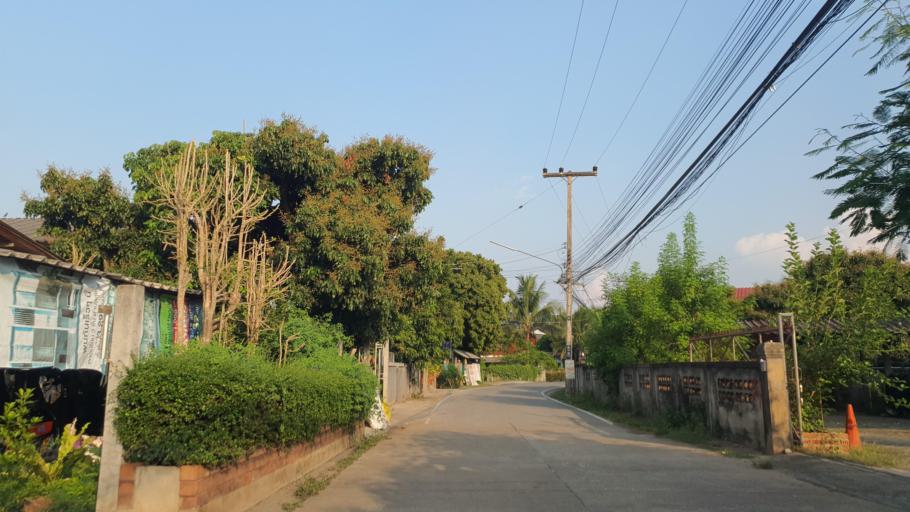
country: TH
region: Chiang Mai
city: San Pa Tong
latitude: 18.6386
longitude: 98.8605
